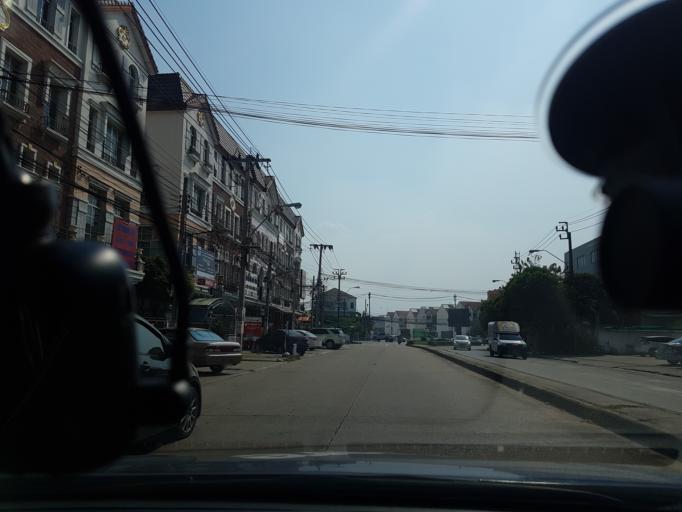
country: TH
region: Bangkok
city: Khan Na Yao
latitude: 13.8417
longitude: 100.6975
